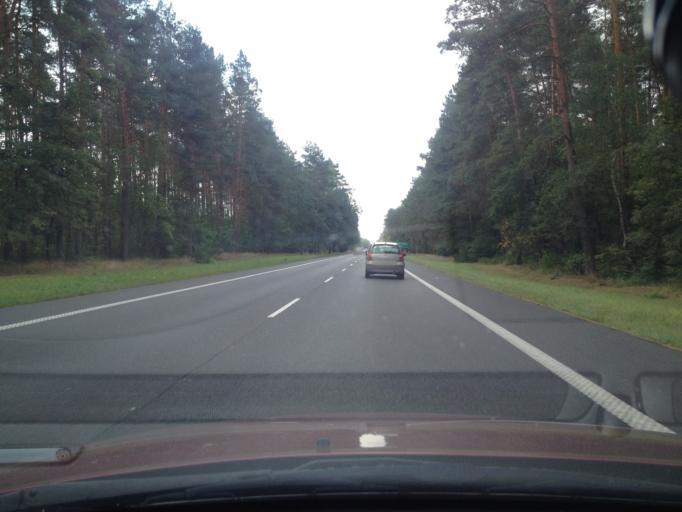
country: PL
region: West Pomeranian Voivodeship
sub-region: Powiat goleniowski
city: Goleniow
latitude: 53.6527
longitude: 14.8161
